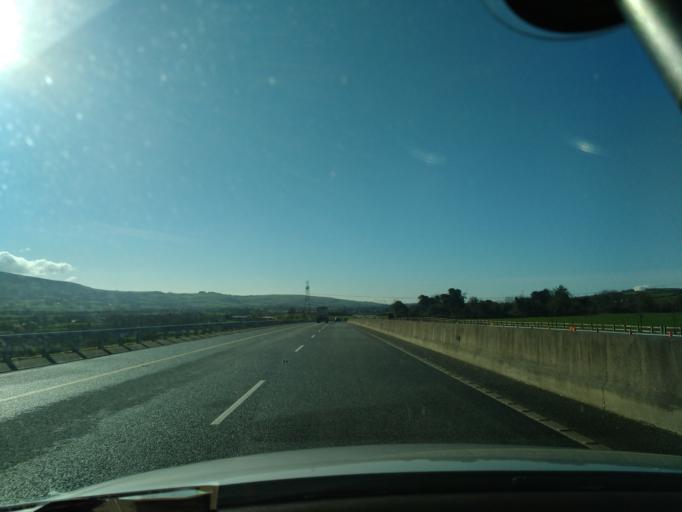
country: IE
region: Munster
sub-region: North Tipperary
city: Nenagh
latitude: 52.8327
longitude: -8.2906
